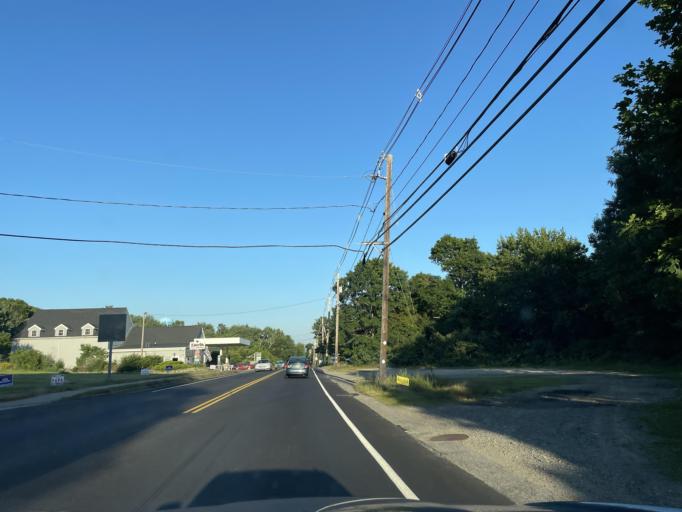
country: US
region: Massachusetts
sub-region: Plymouth County
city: Halifax
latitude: 41.9931
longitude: -70.8701
